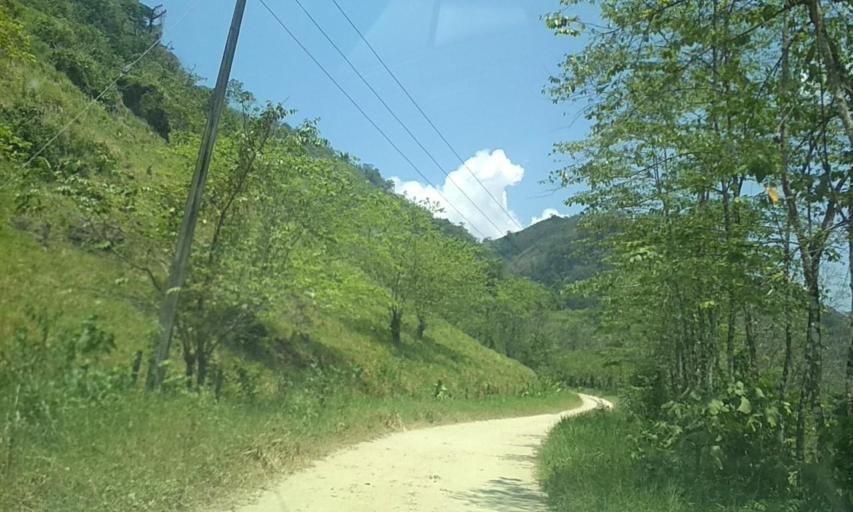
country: MX
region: Chiapas
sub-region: Tecpatan
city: Raudales Malpaso
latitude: 17.2816
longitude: -93.8256
